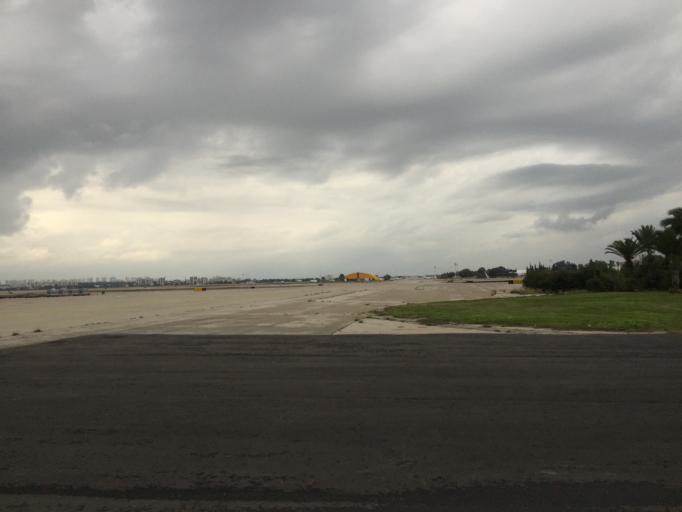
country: IL
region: Central District
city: Yehud
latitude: 31.9958
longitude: 34.8938
